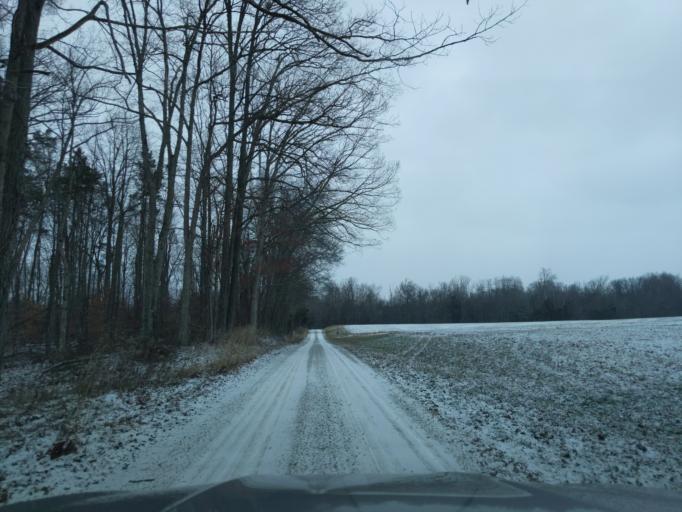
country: US
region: Indiana
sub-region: Decatur County
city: Westport
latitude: 39.2065
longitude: -85.4445
